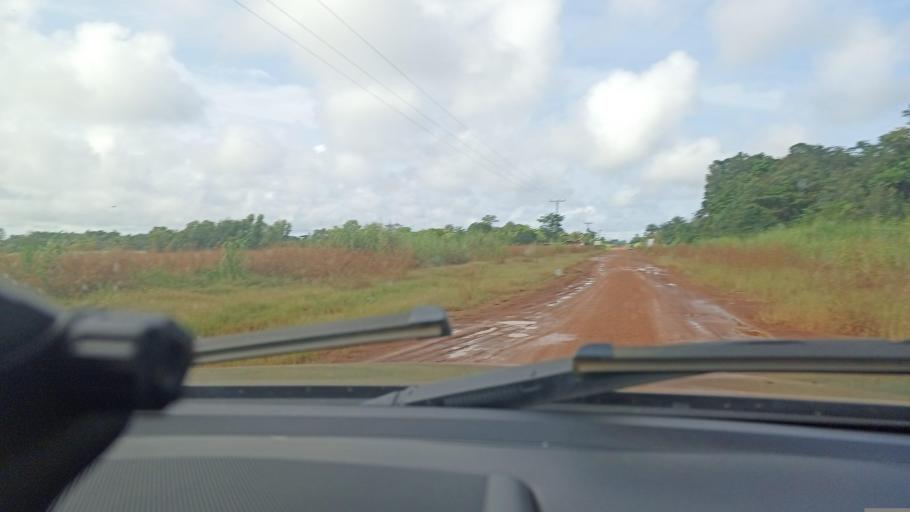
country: LR
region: Grand Cape Mount
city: Robertsport
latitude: 6.6961
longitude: -11.1024
